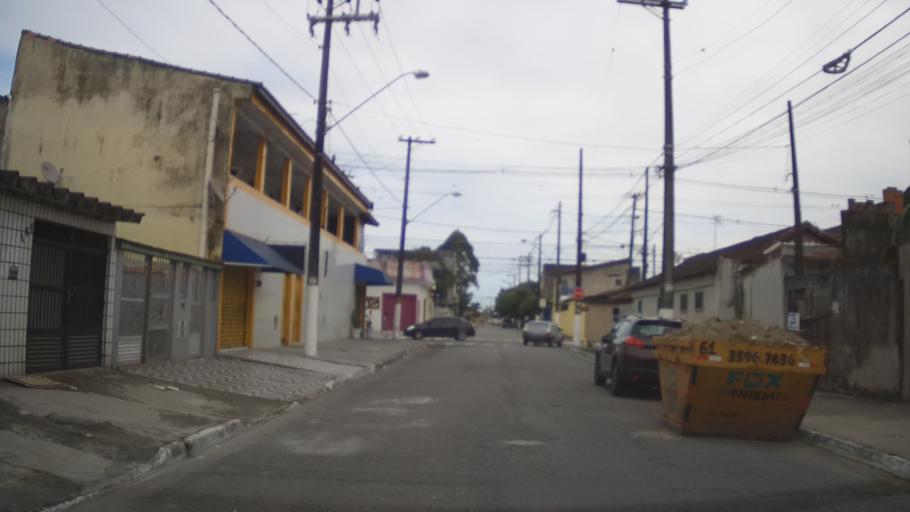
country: BR
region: Sao Paulo
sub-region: Praia Grande
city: Praia Grande
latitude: -24.0241
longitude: -46.4948
